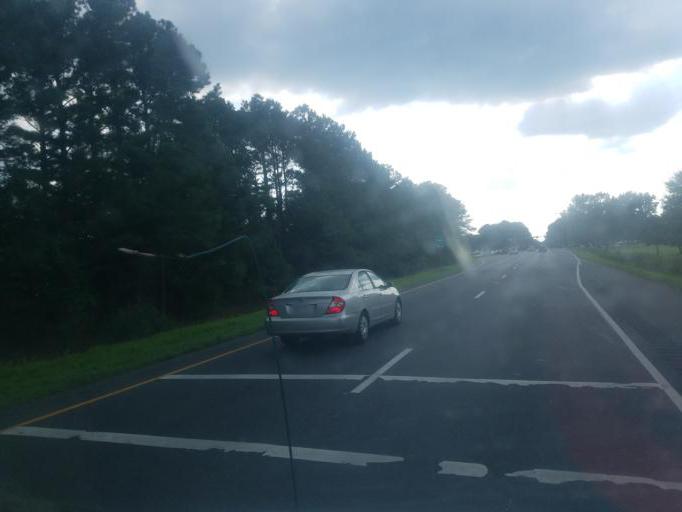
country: US
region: Maryland
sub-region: Wicomico County
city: Pittsville
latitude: 38.3761
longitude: -75.5008
